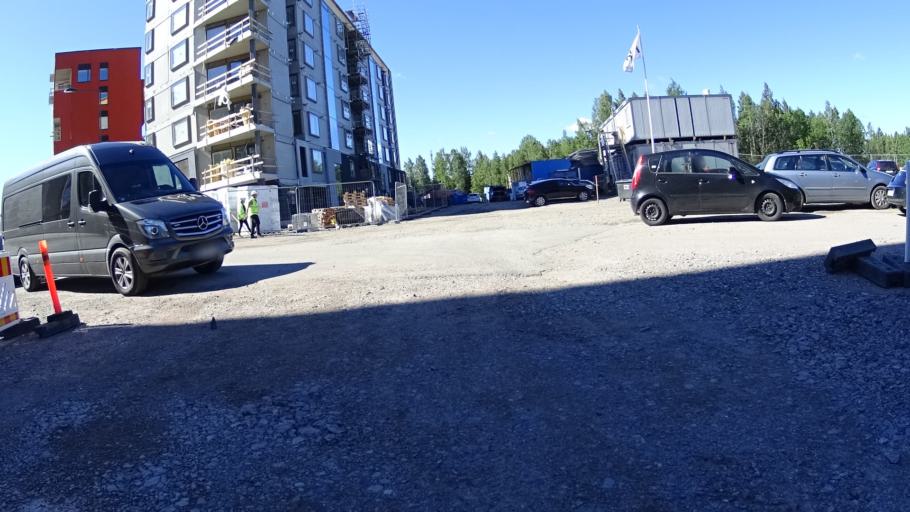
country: FI
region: Uusimaa
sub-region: Helsinki
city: Kilo
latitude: 60.3187
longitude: 24.8310
